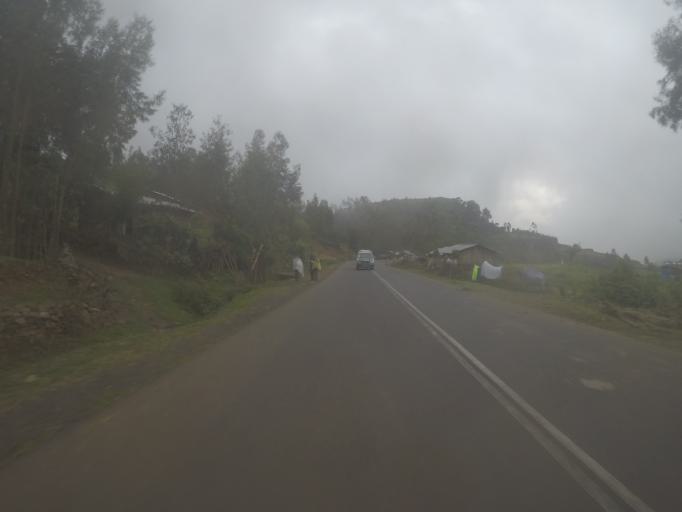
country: ET
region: Amhara
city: Gondar
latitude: 12.7397
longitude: 37.5142
